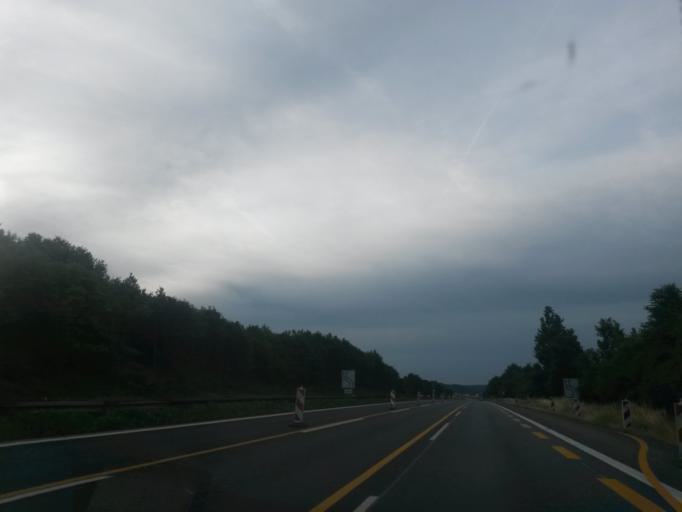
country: DE
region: Bavaria
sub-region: Regierungsbezirk Mittelfranken
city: Greding
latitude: 49.0713
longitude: 11.3029
